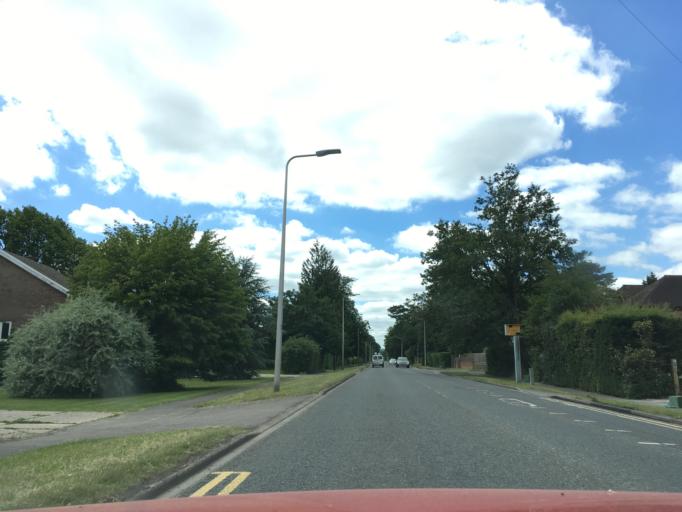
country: GB
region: England
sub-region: West Berkshire
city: Newbury
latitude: 51.3786
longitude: -1.3427
